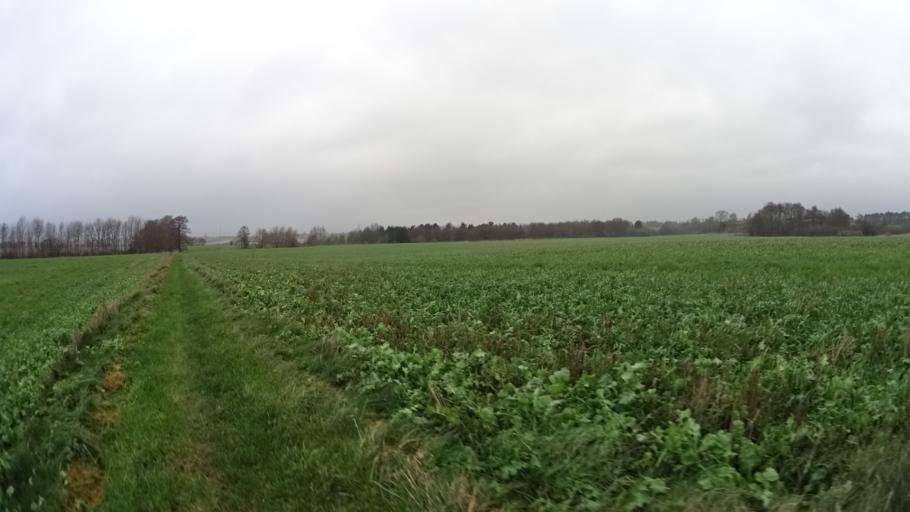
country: DK
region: Central Jutland
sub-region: Arhus Kommune
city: Framlev
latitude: 56.1332
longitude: 10.0243
